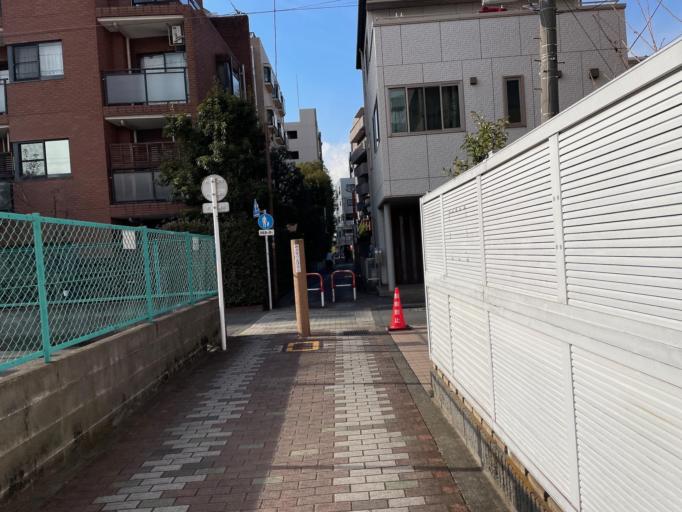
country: JP
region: Tokyo
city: Nishi-Tokyo-shi
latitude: 35.7298
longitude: 139.5412
